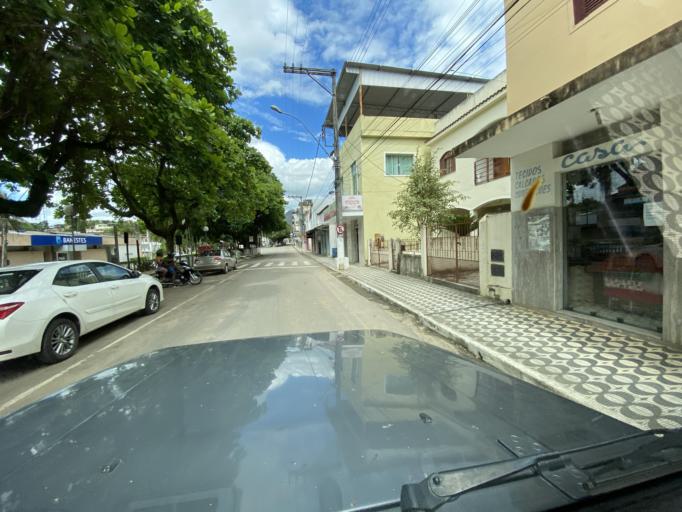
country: BR
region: Espirito Santo
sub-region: Jeronimo Monteiro
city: Jeronimo Monteiro
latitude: -20.7889
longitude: -41.3952
